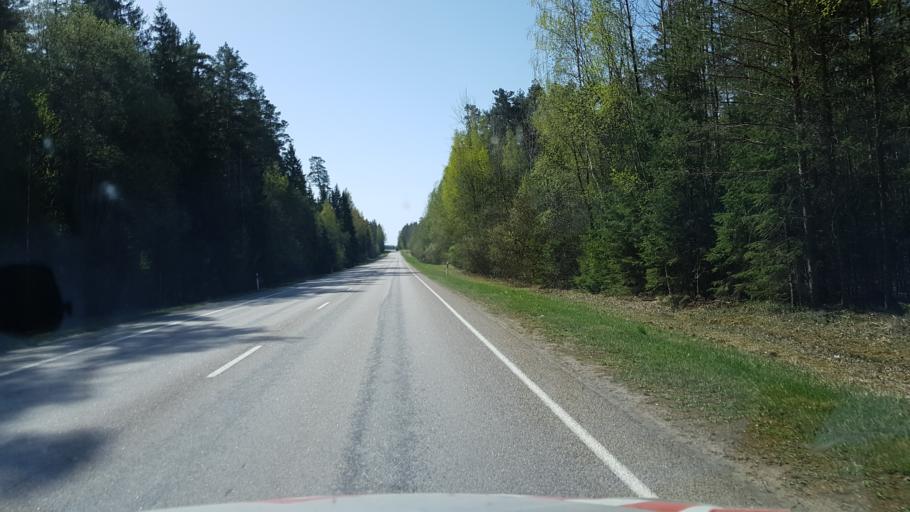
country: EE
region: Valgamaa
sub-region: Valga linn
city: Valga
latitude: 57.8521
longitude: 26.0592
